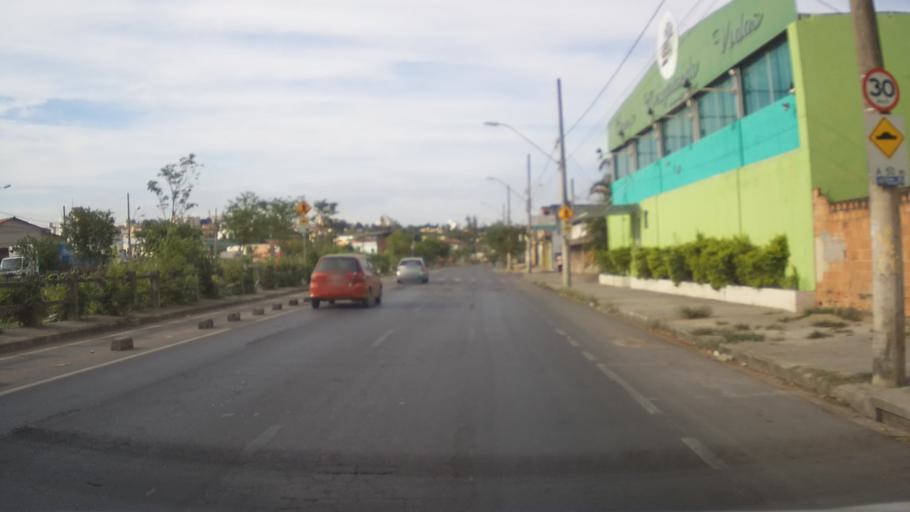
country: BR
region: Minas Gerais
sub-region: Contagem
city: Contagem
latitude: -19.8702
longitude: -44.0121
